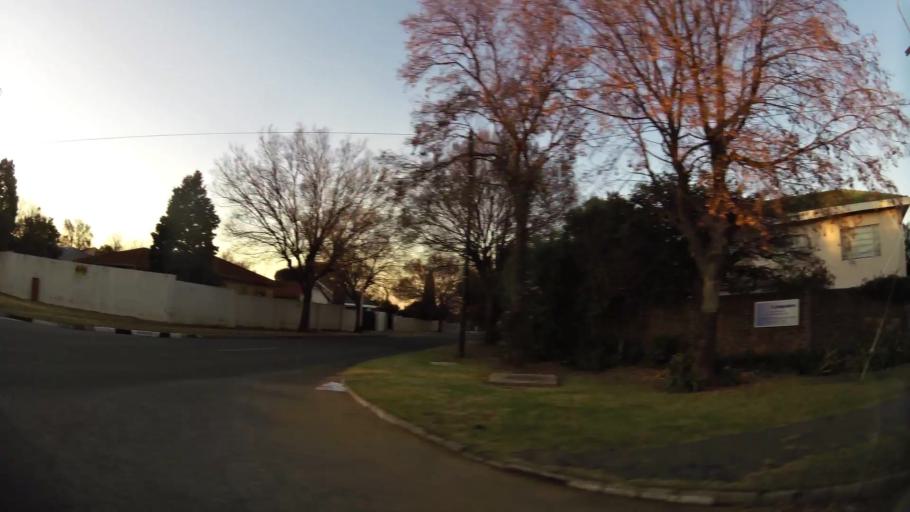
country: ZA
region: Gauteng
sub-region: City of Johannesburg Metropolitan Municipality
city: Roodepoort
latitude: -26.1557
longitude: 27.8949
